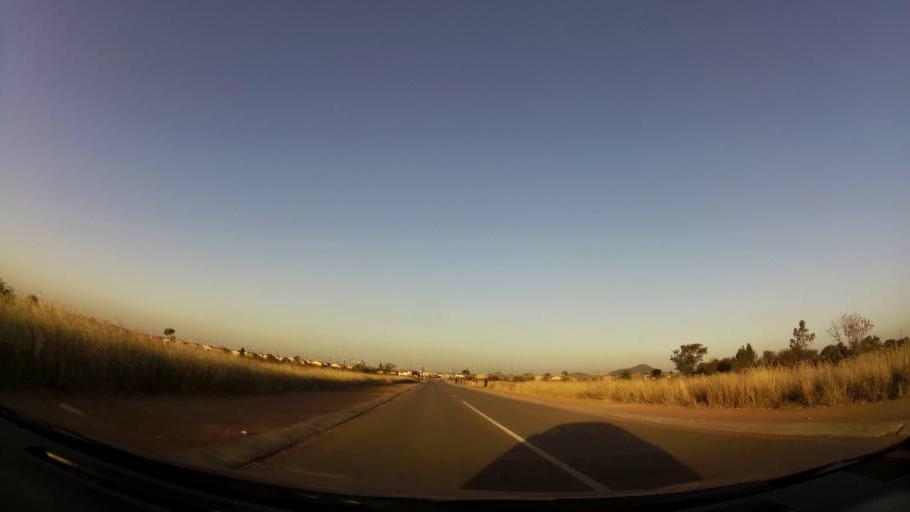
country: ZA
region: North-West
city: Ga-Rankuwa
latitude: -25.6036
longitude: 28.0951
